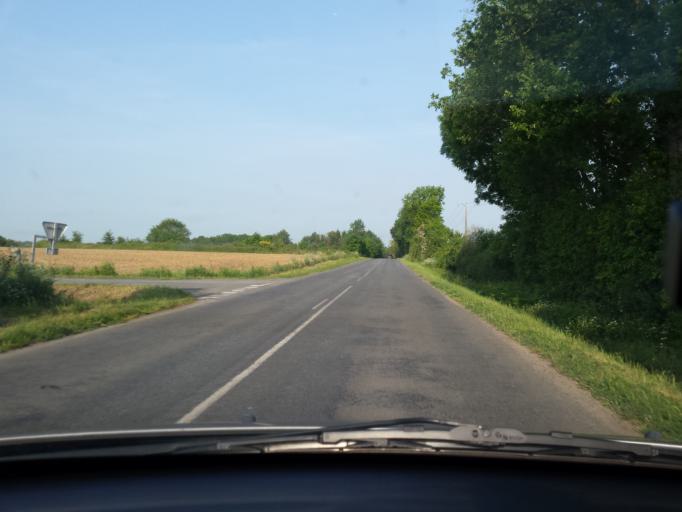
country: FR
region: Pays de la Loire
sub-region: Departement de la Loire-Atlantique
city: Lege
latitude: 46.8836
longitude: -1.6117
